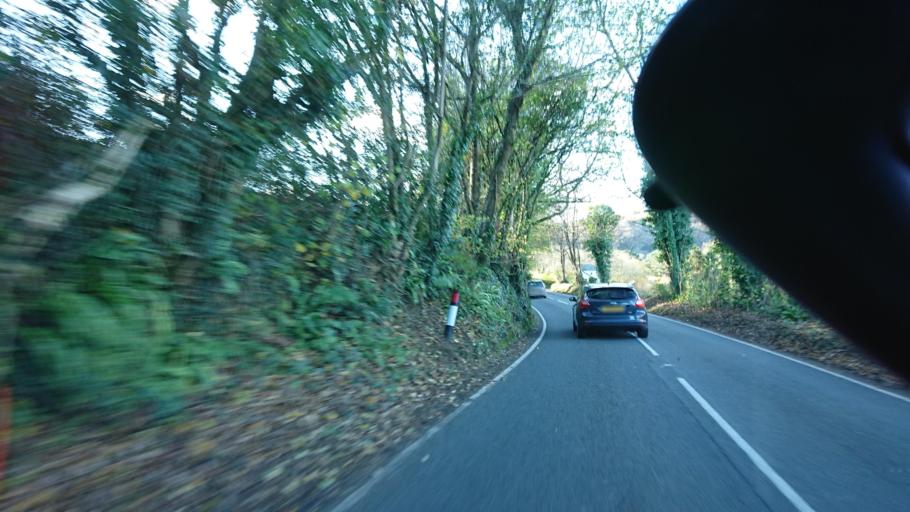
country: GB
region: England
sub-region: Cornwall
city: Looe
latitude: 50.3919
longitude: -4.3763
